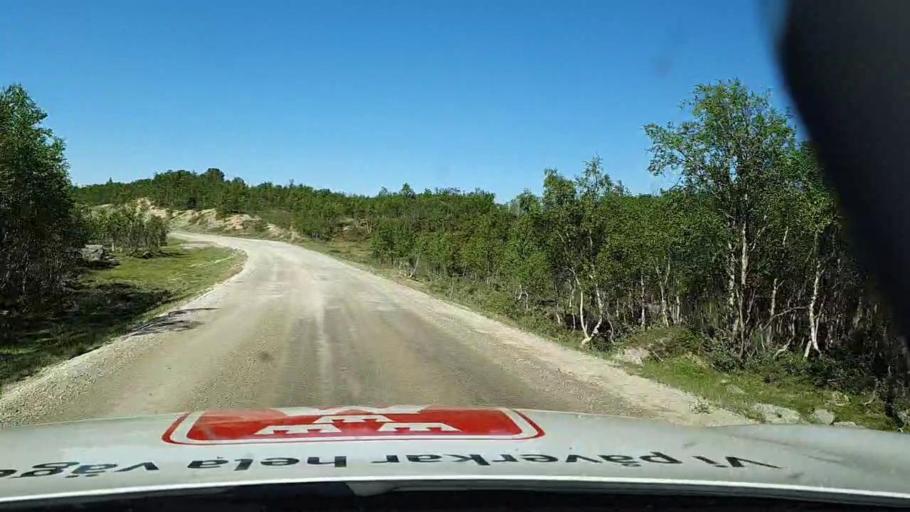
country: SE
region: Jaemtland
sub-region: Are Kommun
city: Are
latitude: 62.6174
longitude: 12.6290
